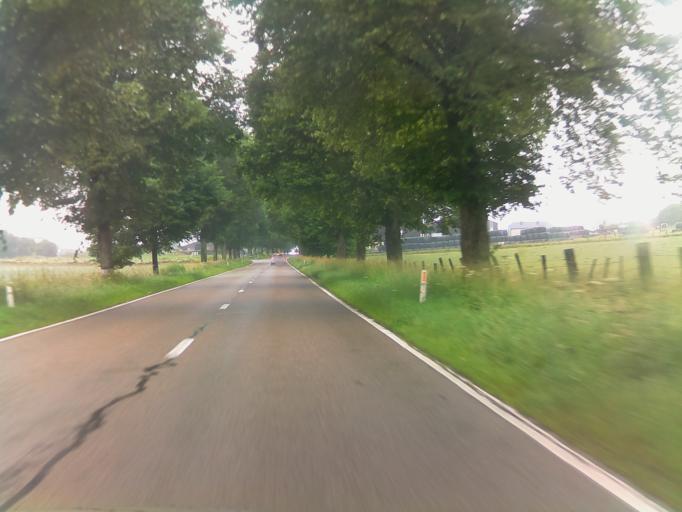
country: BE
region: Wallonia
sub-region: Province du Luxembourg
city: Neufchateau
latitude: 49.8430
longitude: 5.3481
